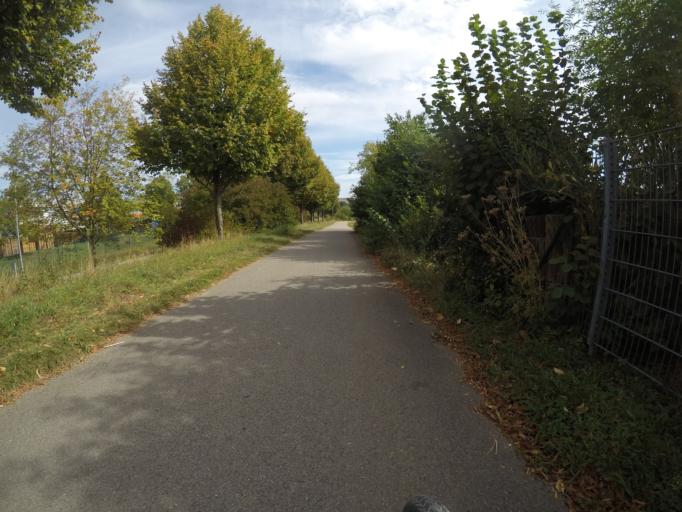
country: DE
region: Baden-Wuerttemberg
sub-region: Regierungsbezirk Stuttgart
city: Vaihingen an der Enz
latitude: 48.9254
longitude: 8.9677
